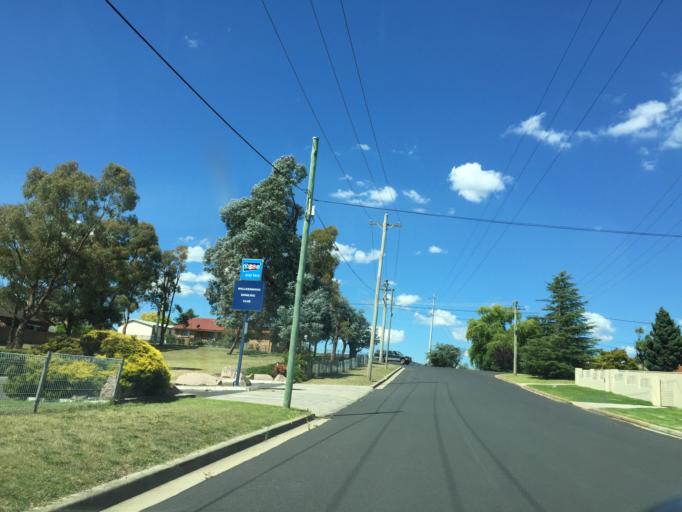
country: AU
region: New South Wales
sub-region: Lithgow
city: Lithgow
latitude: -33.4126
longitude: 150.0657
